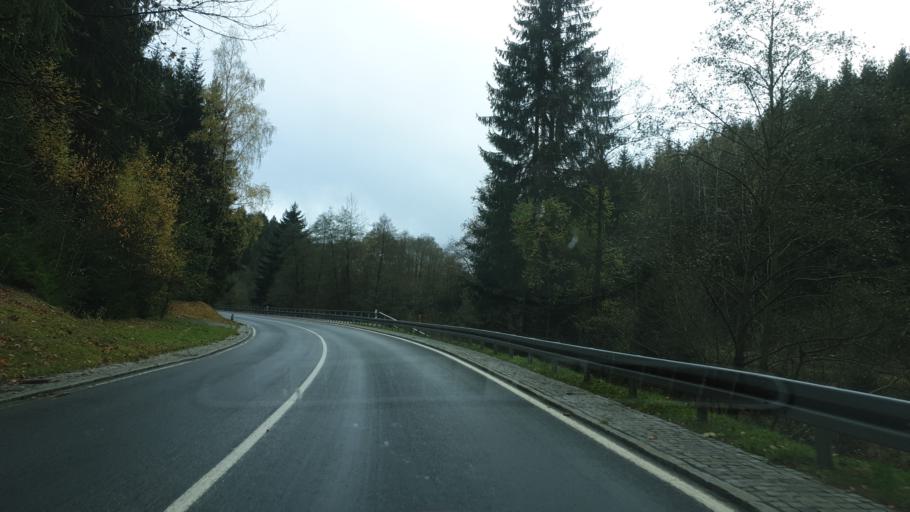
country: DE
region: Saxony
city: Schoenheide
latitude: 50.4995
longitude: 12.5516
